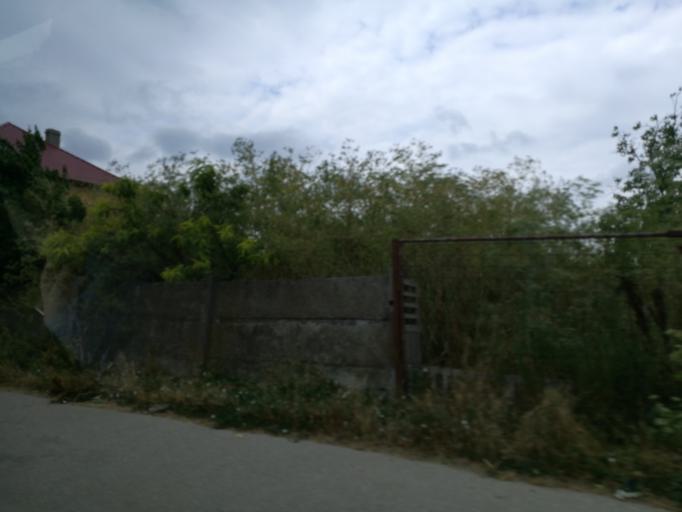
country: RO
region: Constanta
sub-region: Municipiul Mangalia
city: Mangalia
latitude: 43.8171
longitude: 28.5736
